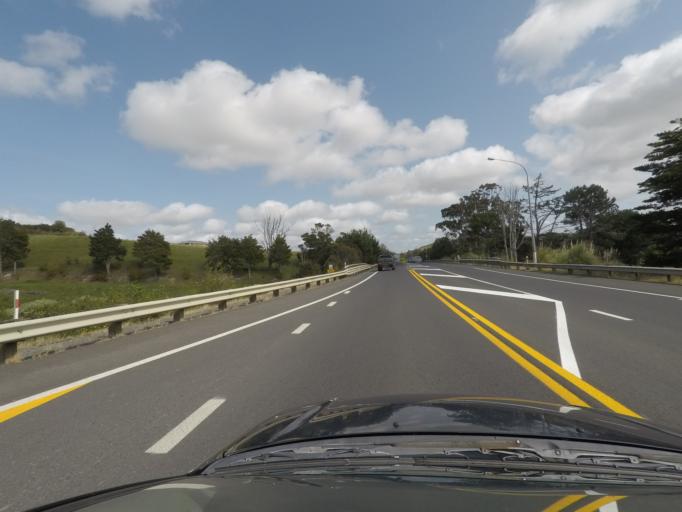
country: NZ
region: Northland
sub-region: Whangarei
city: Whangarei
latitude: -35.8326
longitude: 174.3153
